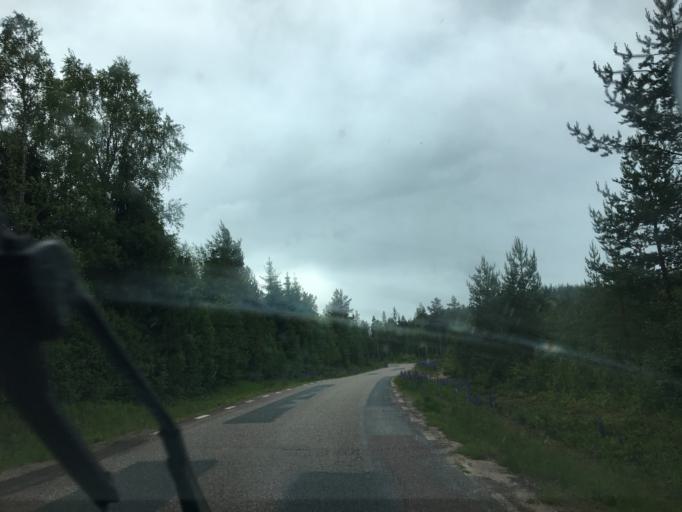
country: SE
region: OErebro
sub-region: Hallefors Kommun
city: Haellefors
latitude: 60.0940
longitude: 14.4772
